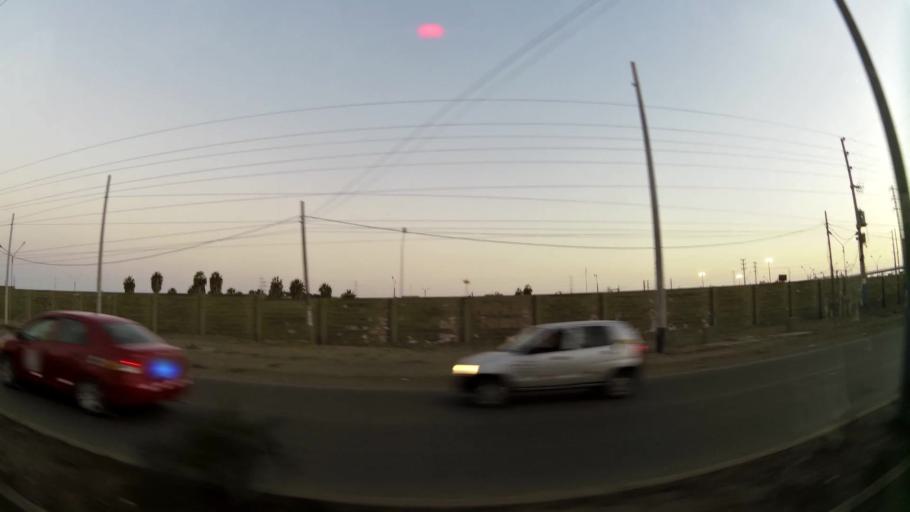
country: PE
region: Ica
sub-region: Provincia de Pisco
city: Pisco
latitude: -13.7111
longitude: -76.1937
